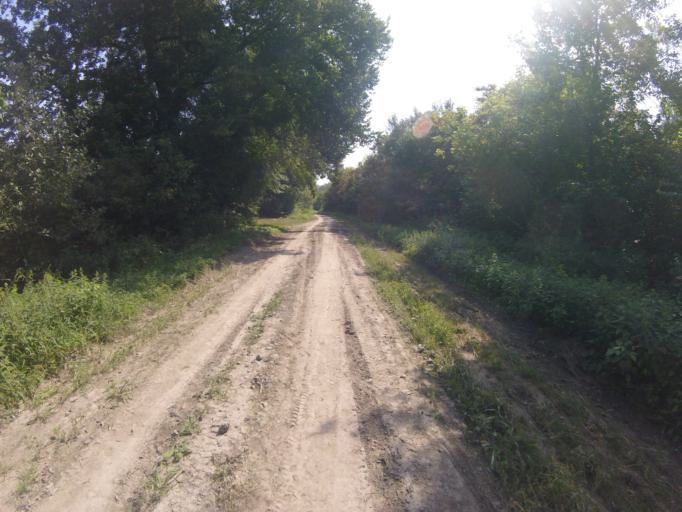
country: HU
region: Bacs-Kiskun
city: Baja
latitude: 46.1967
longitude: 18.9049
